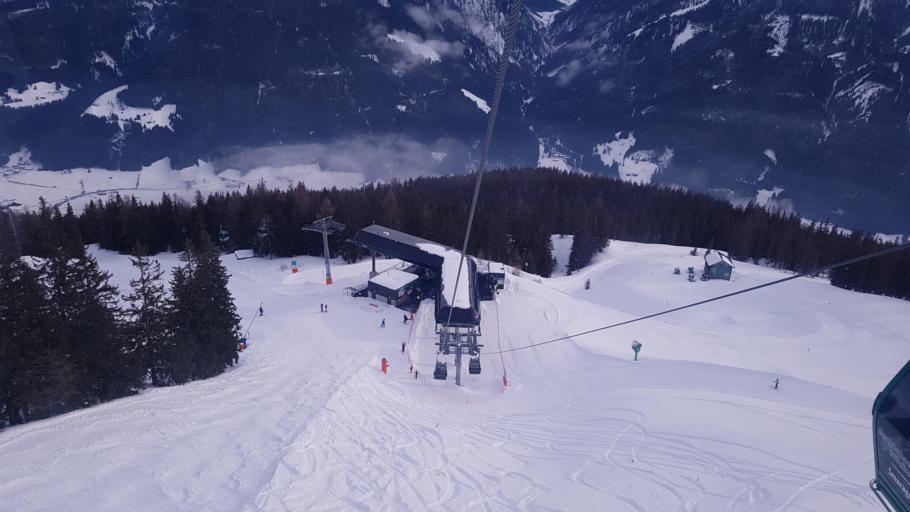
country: AT
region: Salzburg
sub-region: Politischer Bezirk Zell am See
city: Neukirchen am Grossvenediger
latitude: 47.2734
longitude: 12.3026
